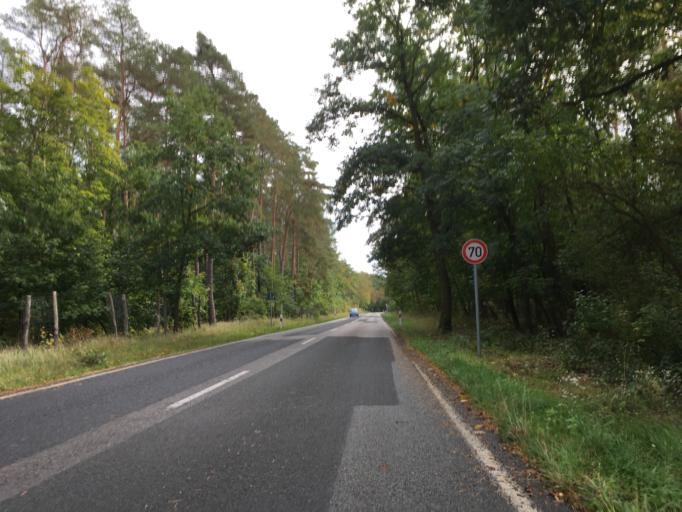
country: DE
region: Brandenburg
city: Oderberg
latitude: 52.8914
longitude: 14.0628
